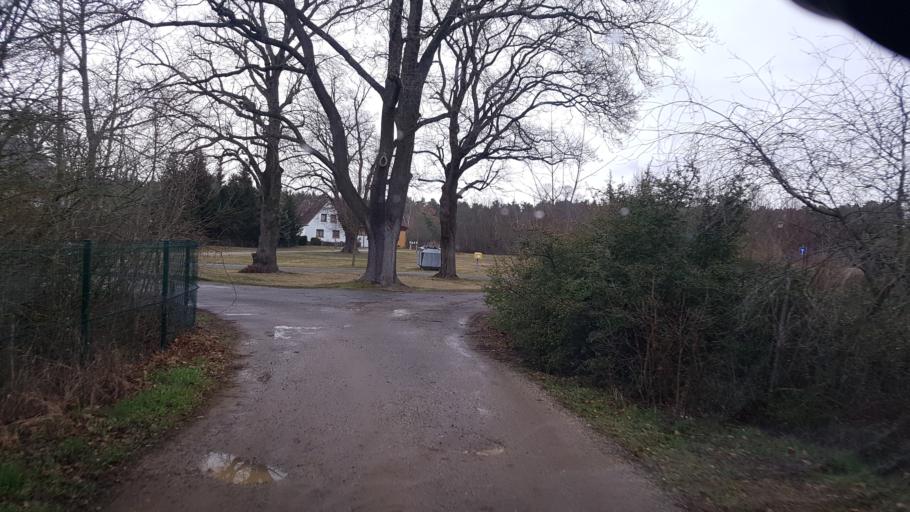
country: DE
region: Brandenburg
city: Sallgast
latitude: 51.6656
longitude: 13.8256
